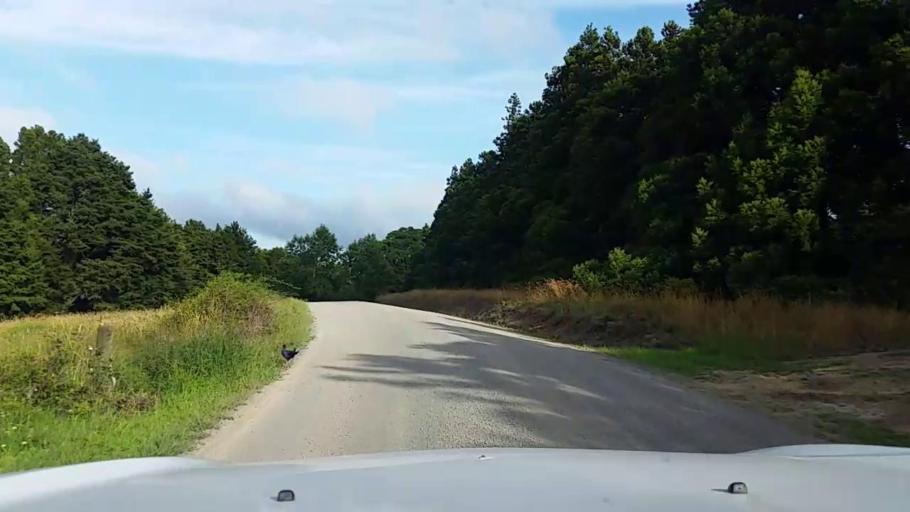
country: NZ
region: Northland
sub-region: Whangarei
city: Maungatapere
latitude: -35.6778
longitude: 174.1781
